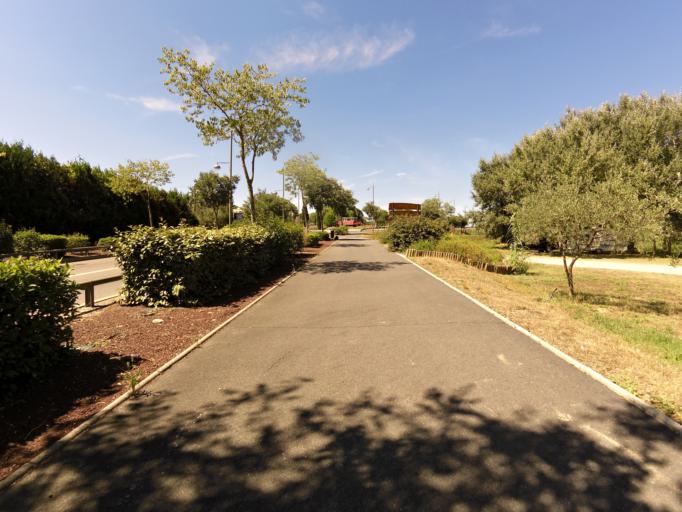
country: FR
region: Languedoc-Roussillon
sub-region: Departement du Gard
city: Sommieres
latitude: 43.7880
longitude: 4.0828
